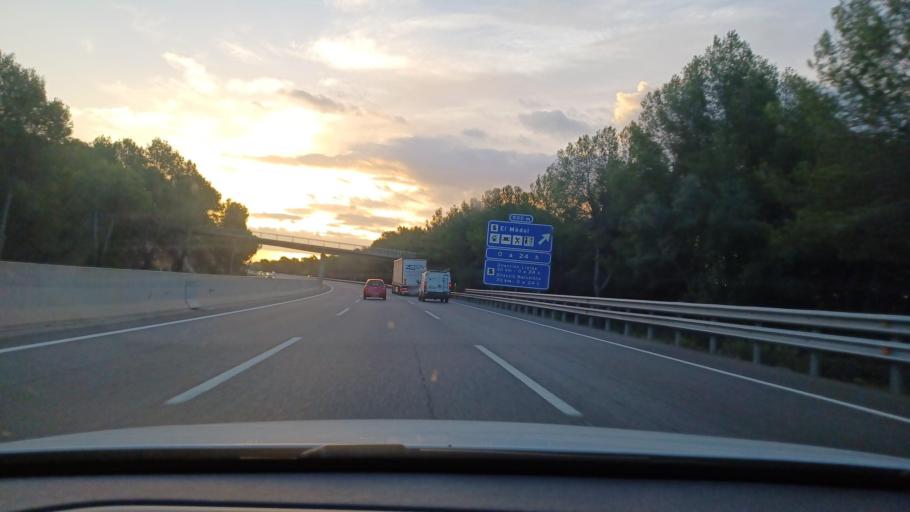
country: ES
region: Catalonia
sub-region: Provincia de Tarragona
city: el Catllar
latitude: 41.1372
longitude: 1.3366
